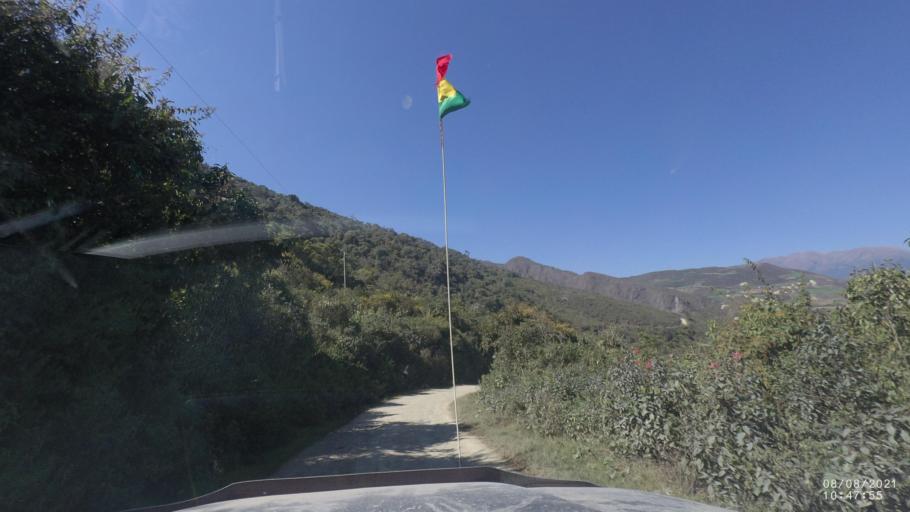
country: BO
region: La Paz
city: Quime
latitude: -16.7137
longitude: -66.7065
